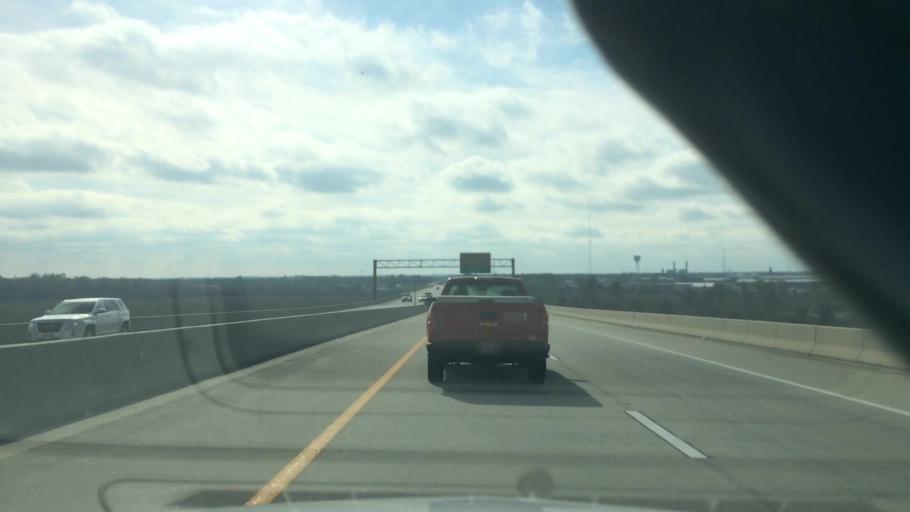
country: US
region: North Carolina
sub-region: New Hanover County
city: Wrightsboro
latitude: 34.2970
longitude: -77.9617
